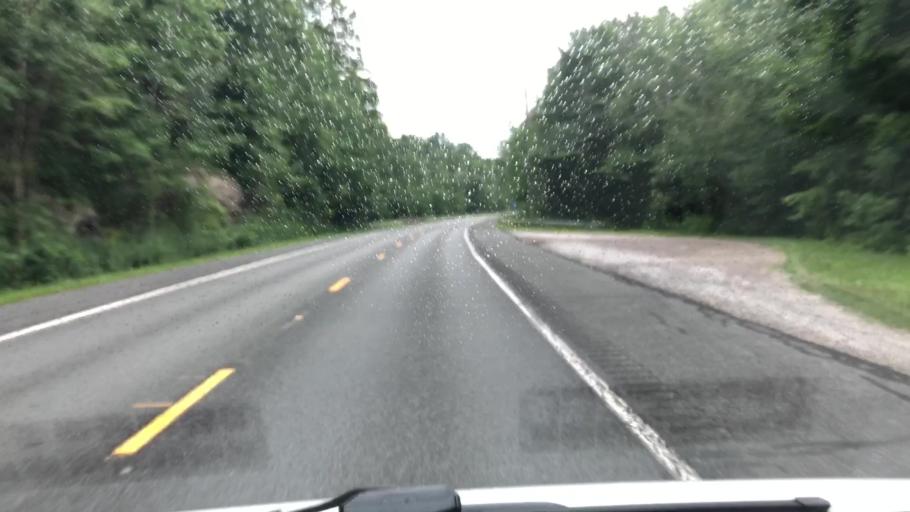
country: US
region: Massachusetts
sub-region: Berkshire County
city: Lanesborough
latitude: 42.5494
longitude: -73.2342
